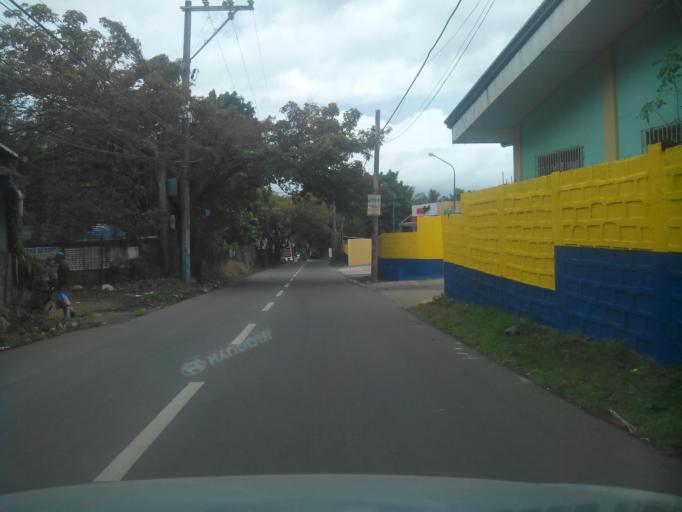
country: PH
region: Calabarzon
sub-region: Province of Rizal
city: Teresa
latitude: 14.5955
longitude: 121.1810
